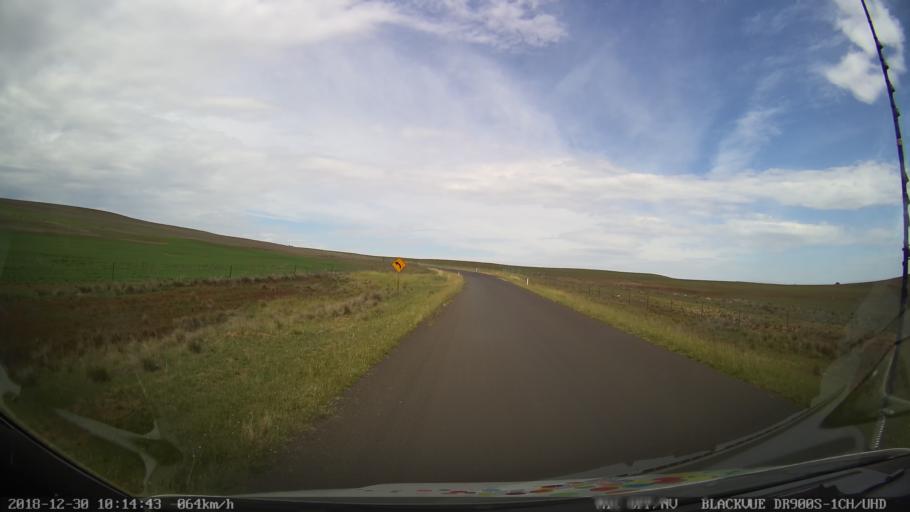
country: AU
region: New South Wales
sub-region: Snowy River
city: Berridale
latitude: -36.5405
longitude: 149.0525
